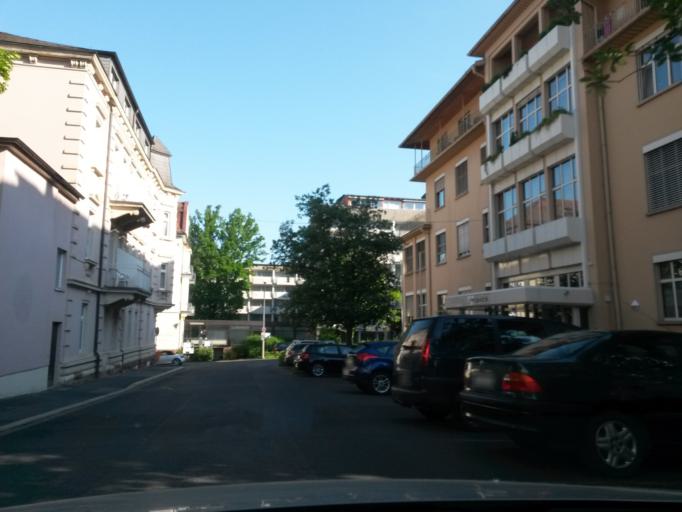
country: DE
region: Bavaria
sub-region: Regierungsbezirk Unterfranken
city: Bad Kissingen
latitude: 50.1973
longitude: 10.0808
